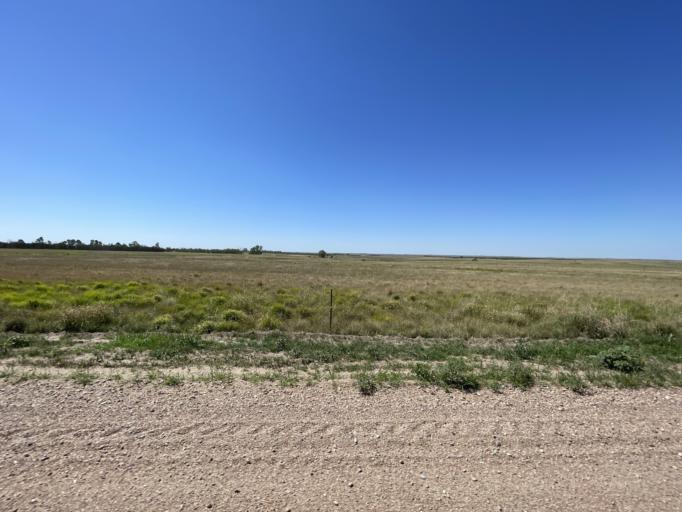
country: US
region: Nebraska
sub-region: Red Willow County
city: McCook
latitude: 40.4375
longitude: -100.7312
